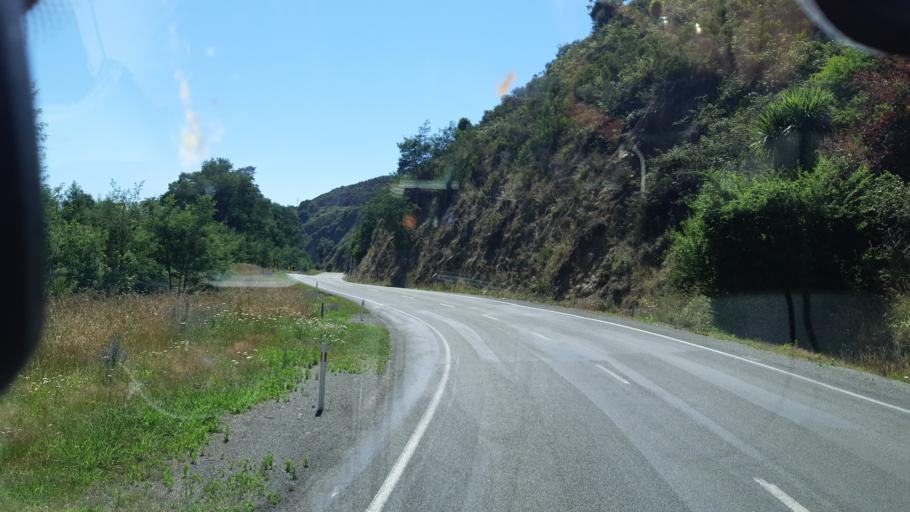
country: NZ
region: Canterbury
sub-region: Kaikoura District
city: Kaikoura
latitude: -42.6340
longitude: 173.3505
